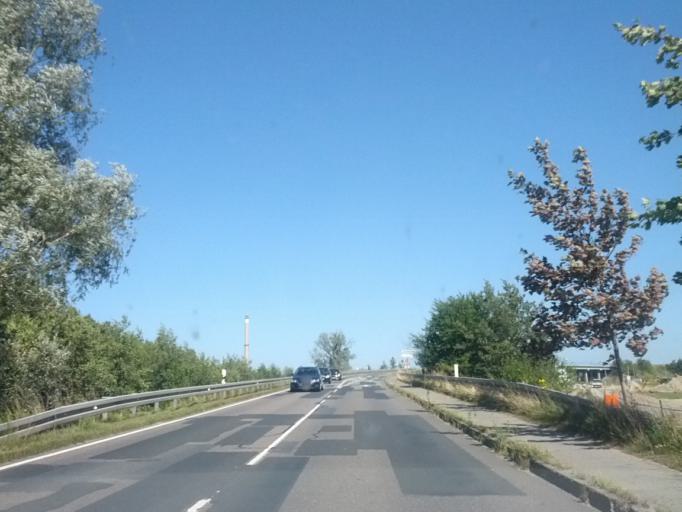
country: DE
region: Mecklenburg-Vorpommern
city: Sagard
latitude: 54.4853
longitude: 13.5772
